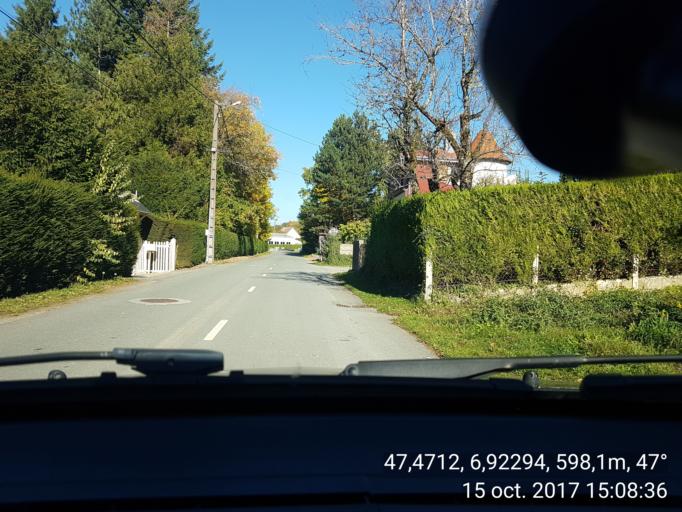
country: FR
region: Franche-Comte
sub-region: Territoire de Belfort
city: Beaucourt
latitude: 47.4713
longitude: 6.9227
